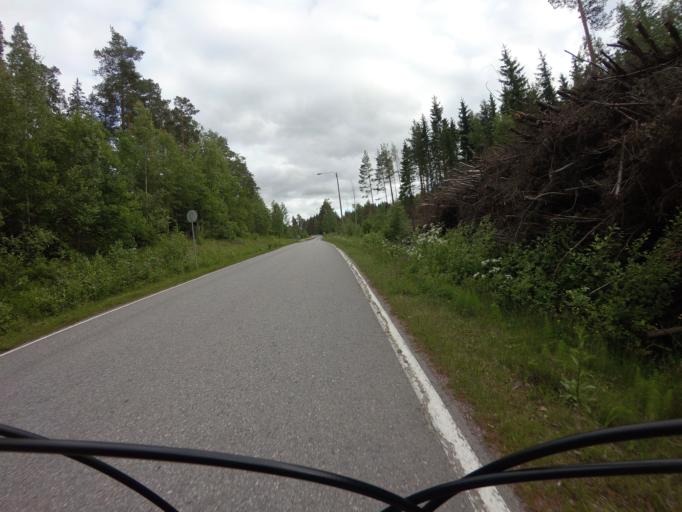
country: FI
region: Varsinais-Suomi
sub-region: Turku
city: Lieto
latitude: 60.5135
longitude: 22.3822
